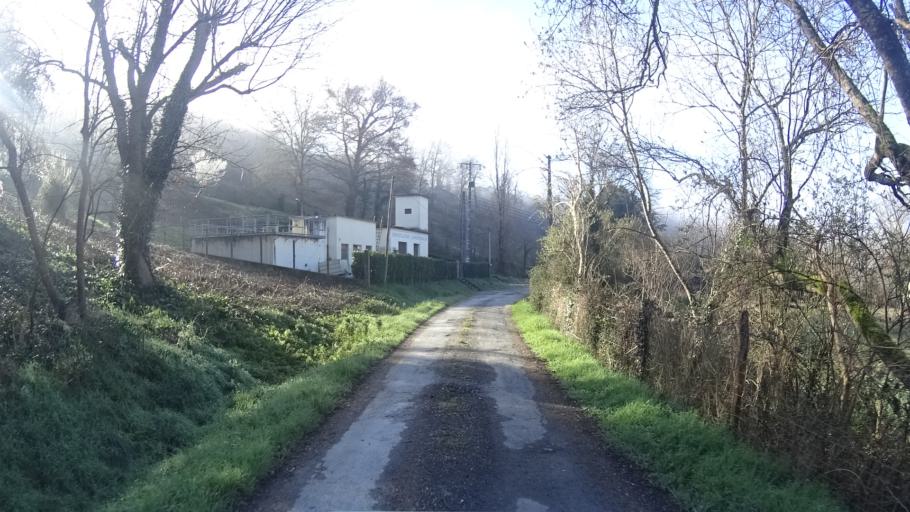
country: FR
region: Aquitaine
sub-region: Departement de la Dordogne
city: La Roche-Chalais
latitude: 45.1543
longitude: 0.0062
